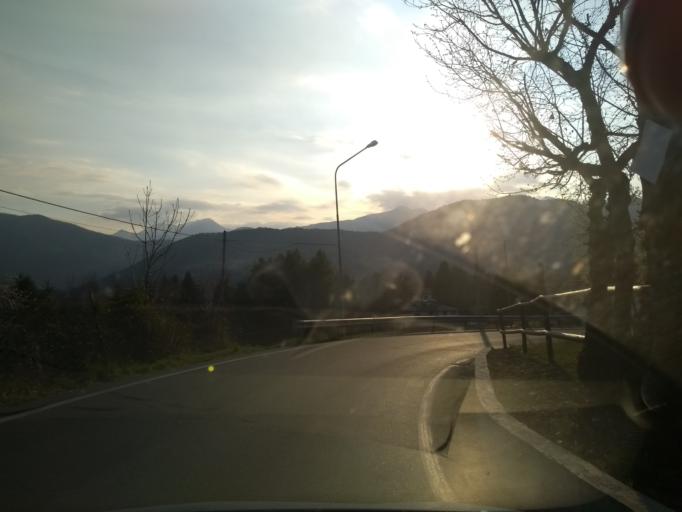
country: IT
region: Piedmont
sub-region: Provincia di Torino
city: Lanzo Torinese
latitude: 45.2801
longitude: 7.4872
